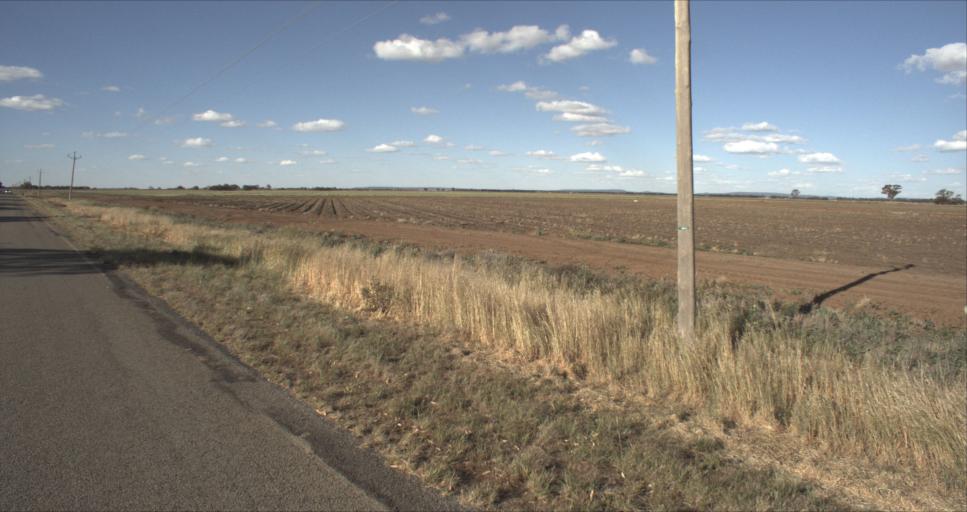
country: AU
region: New South Wales
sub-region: Leeton
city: Leeton
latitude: -34.5513
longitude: 146.2791
